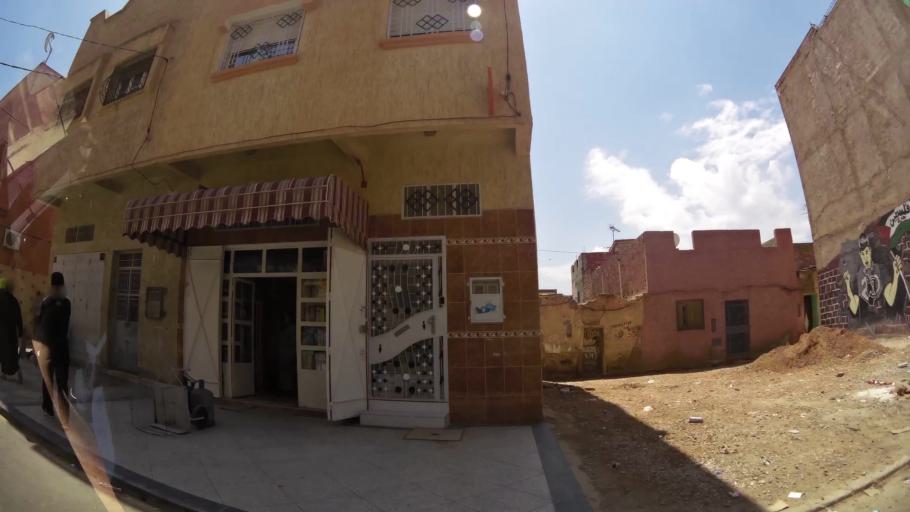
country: MA
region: Oriental
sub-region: Oujda-Angad
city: Oujda
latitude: 34.6828
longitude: -1.9017
